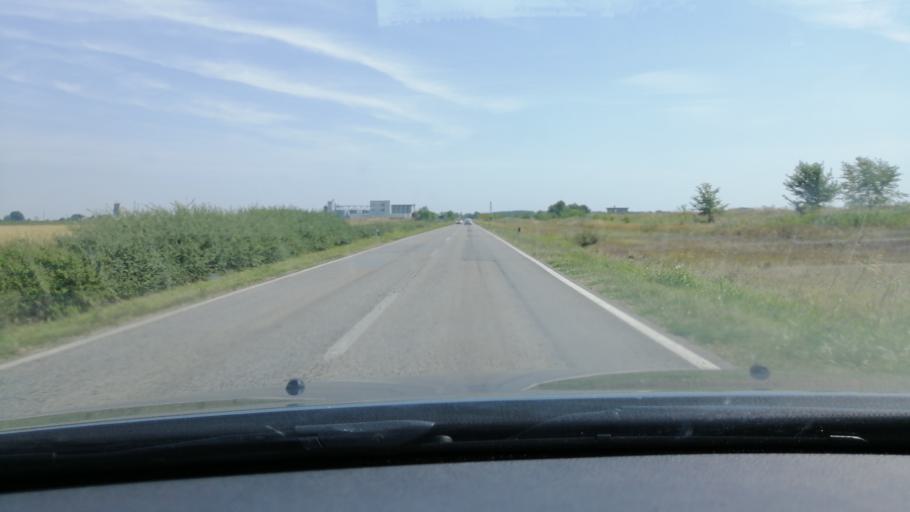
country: RS
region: Autonomna Pokrajina Vojvodina
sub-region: Srednjebanatski Okrug
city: Secanj
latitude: 45.3726
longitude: 20.7470
